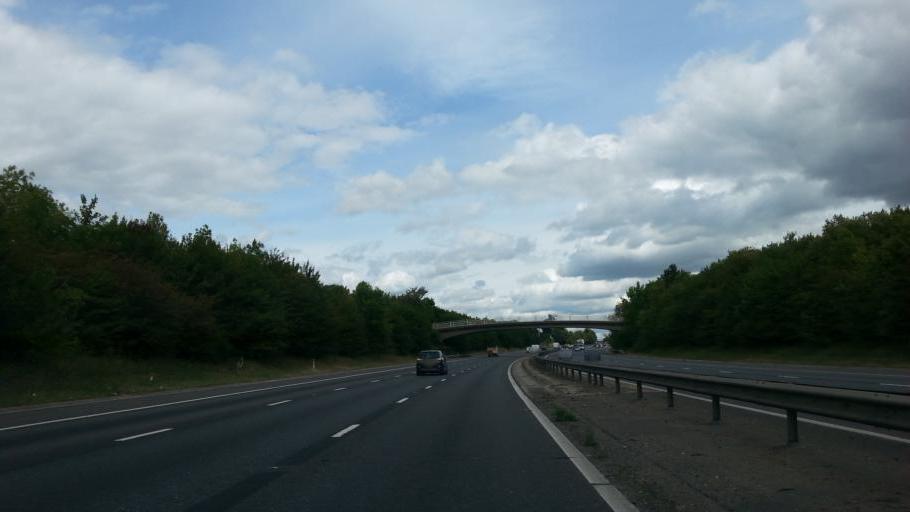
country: GB
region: England
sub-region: Essex
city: Little Hallingbury
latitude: 51.8084
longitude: 0.1773
